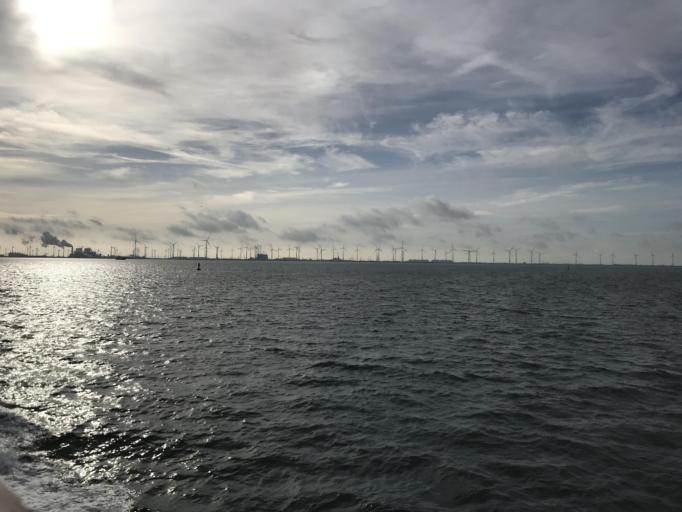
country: DE
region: Lower Saxony
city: Borkum
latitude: 53.4981
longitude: 6.8180
